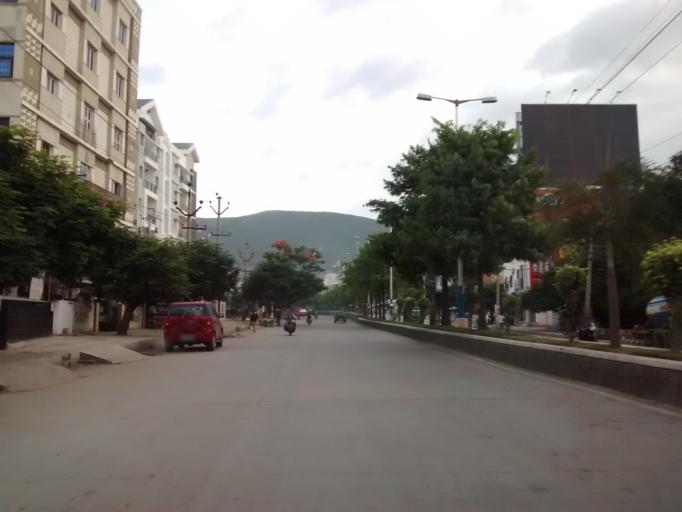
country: IN
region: Andhra Pradesh
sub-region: Chittoor
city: Akkarampalle
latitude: 13.6432
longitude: 79.4276
